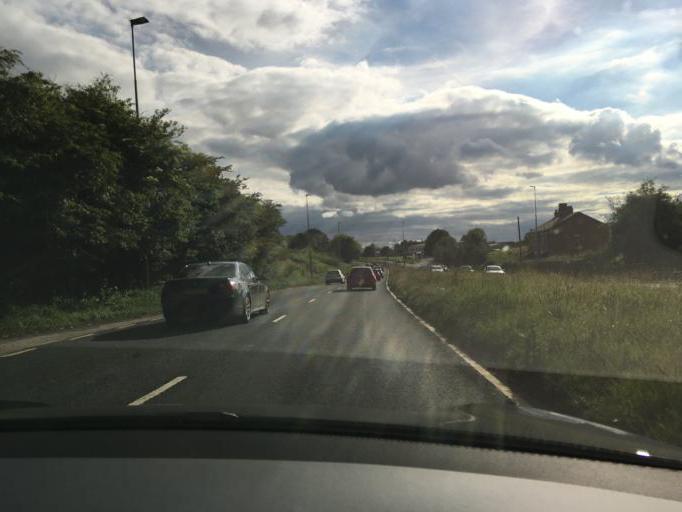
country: GB
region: England
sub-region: Trafford
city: Carrington
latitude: 53.4686
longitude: -2.3877
